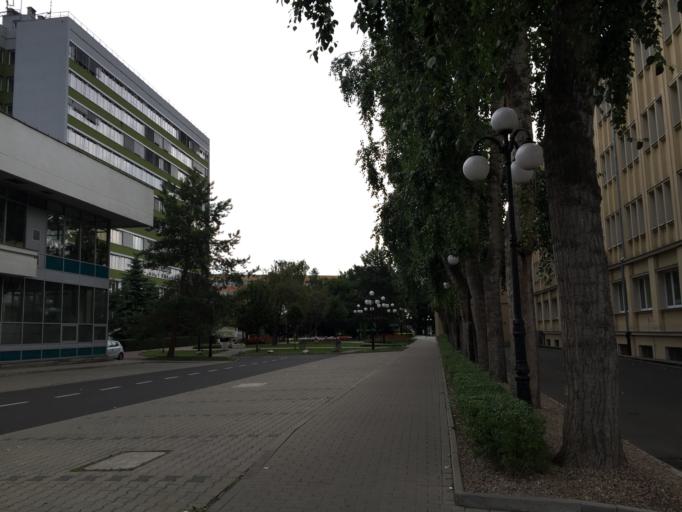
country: PL
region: Lesser Poland Voivodeship
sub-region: Krakow
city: Krakow
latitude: 50.0662
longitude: 19.9172
